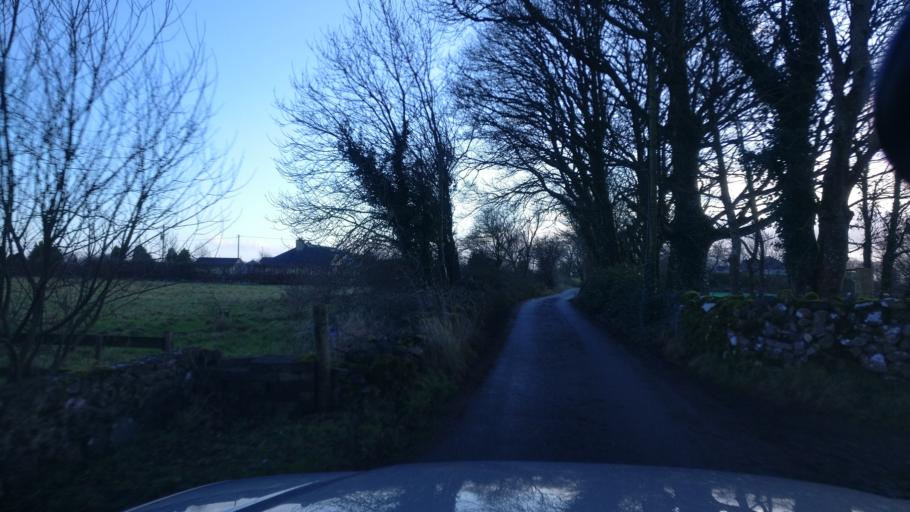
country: IE
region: Connaught
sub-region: County Galway
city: Loughrea
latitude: 53.2367
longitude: -8.5766
